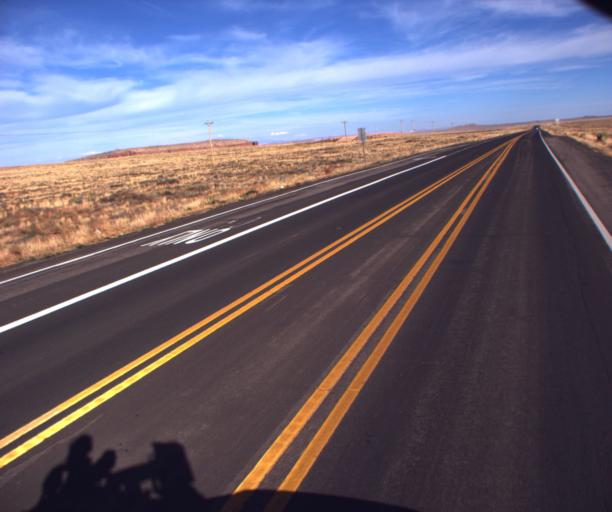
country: US
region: Arizona
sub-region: Apache County
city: Lukachukai
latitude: 36.9596
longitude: -109.3468
